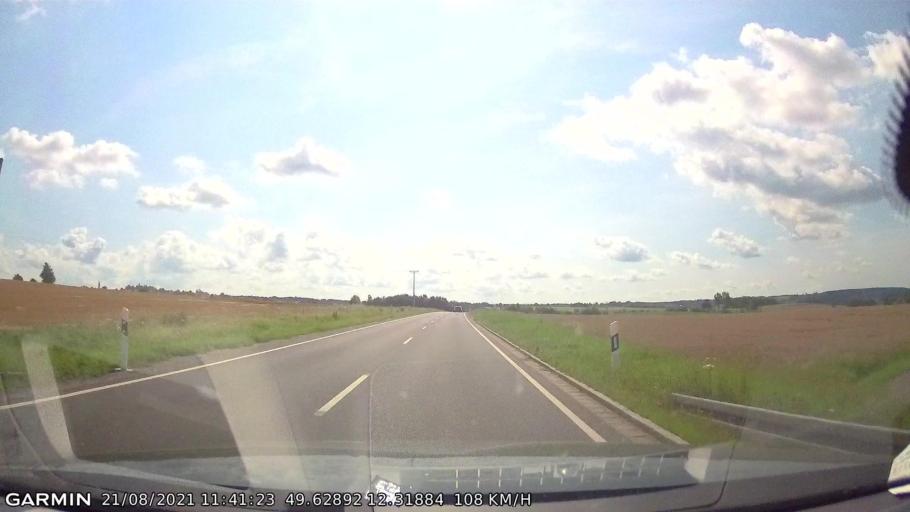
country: DE
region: Bavaria
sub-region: Upper Palatinate
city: Vohenstrauss
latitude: 49.6288
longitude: 12.3190
